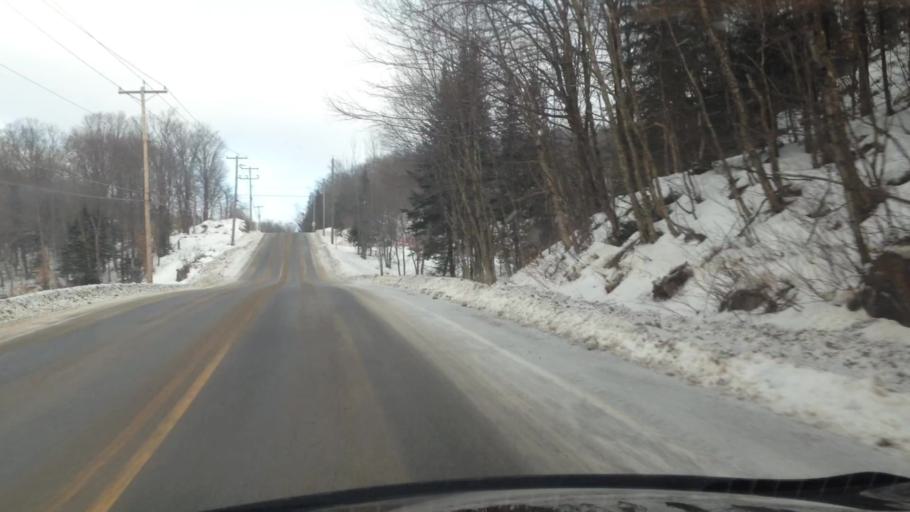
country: CA
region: Quebec
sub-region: Laurentides
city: Sainte-Agathe-des-Monts
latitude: 45.9336
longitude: -74.4513
